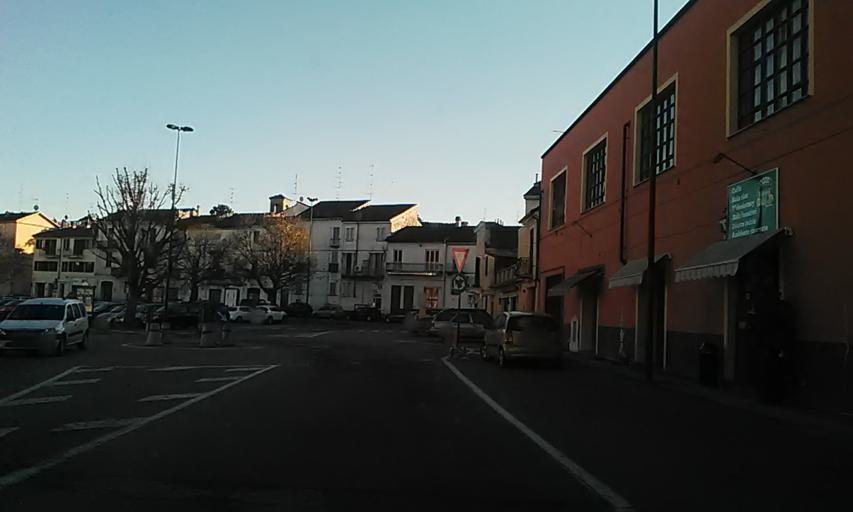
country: IT
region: Piedmont
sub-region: Provincia di Alessandria
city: Casale Monferrato
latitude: 45.1409
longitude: 8.4519
